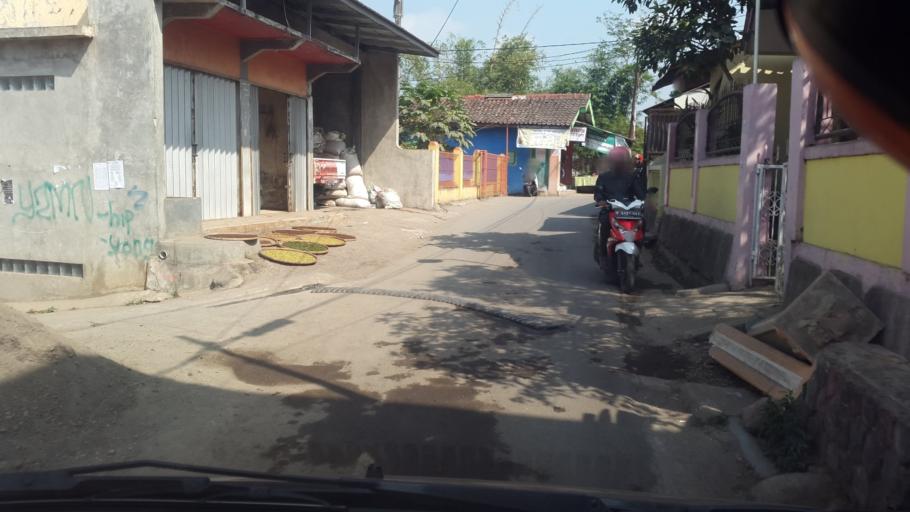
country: ID
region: West Java
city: Sukabumi
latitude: -6.9016
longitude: 106.9017
